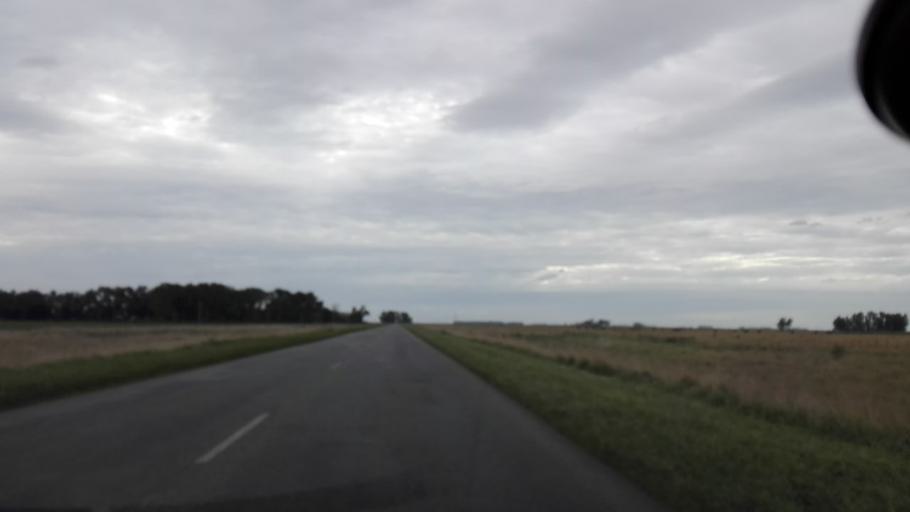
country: AR
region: Buenos Aires
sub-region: Partido de Rauch
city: Rauch
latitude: -36.5296
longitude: -59.0377
